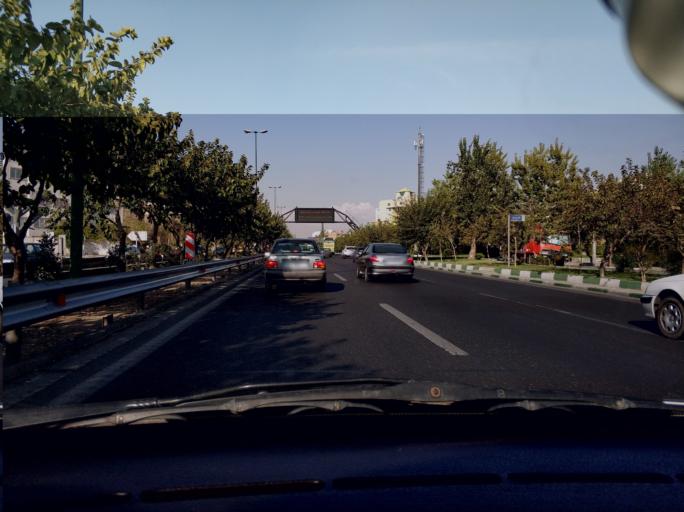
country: IR
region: Tehran
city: Tehran
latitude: 35.7239
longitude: 51.3635
